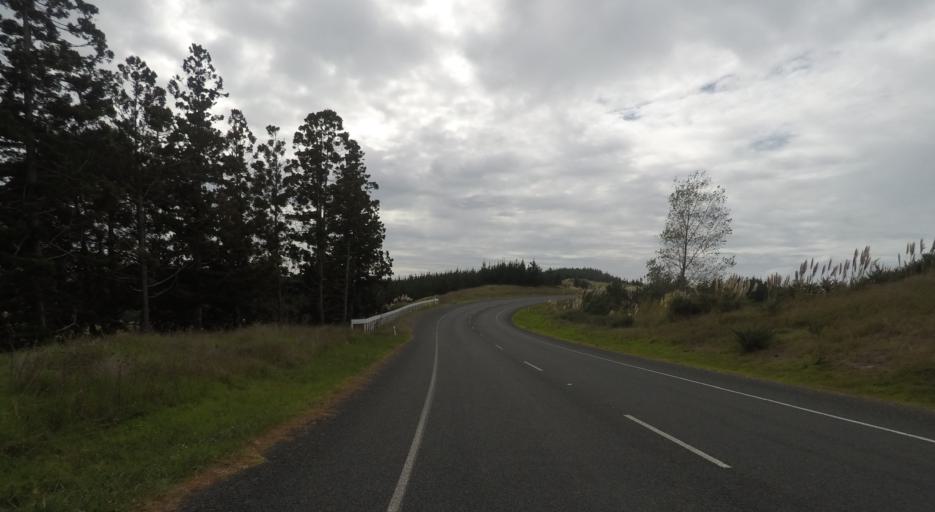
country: NZ
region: Auckland
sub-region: Auckland
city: Rothesay Bay
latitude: -36.6540
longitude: 174.6925
